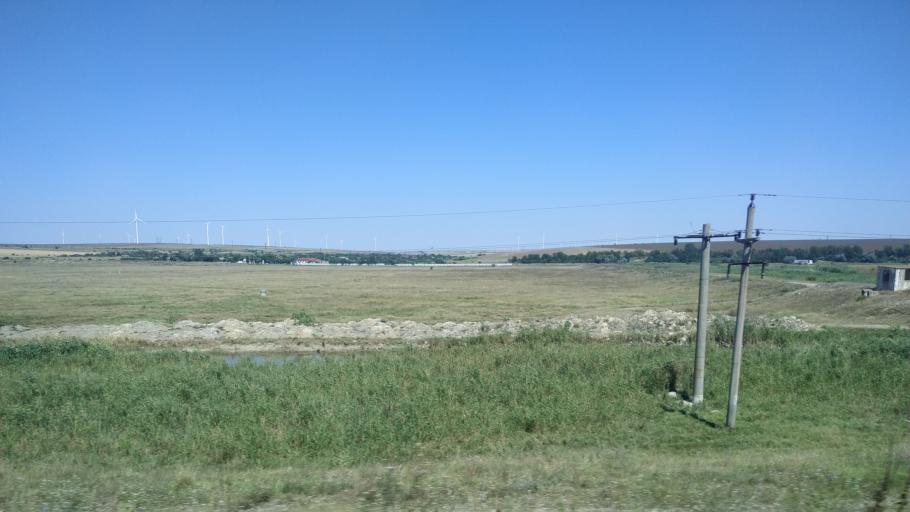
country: RO
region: Constanta
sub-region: Comuna Mircea Voda
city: Mircea Voda
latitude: 44.2636
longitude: 28.1735
